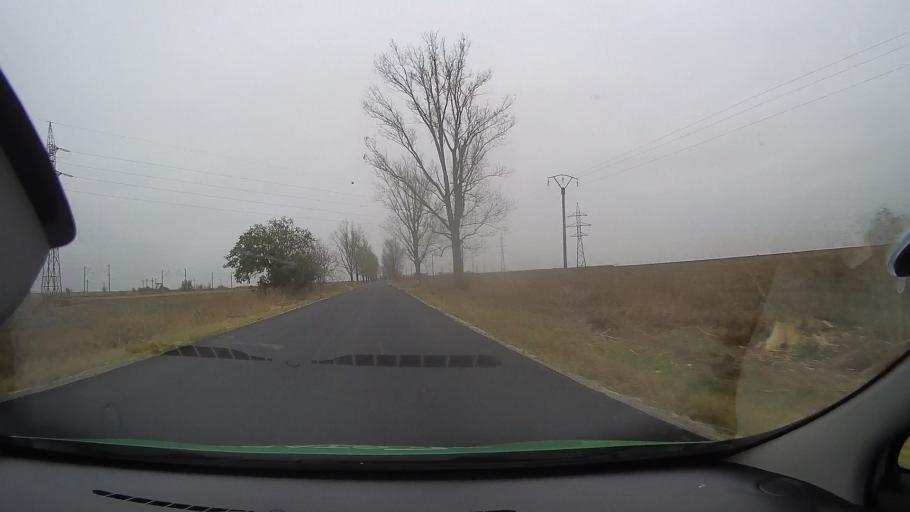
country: RO
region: Ialomita
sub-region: Comuna Valea Ciorii
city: Valea Ciorii
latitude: 44.7523
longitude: 27.5671
